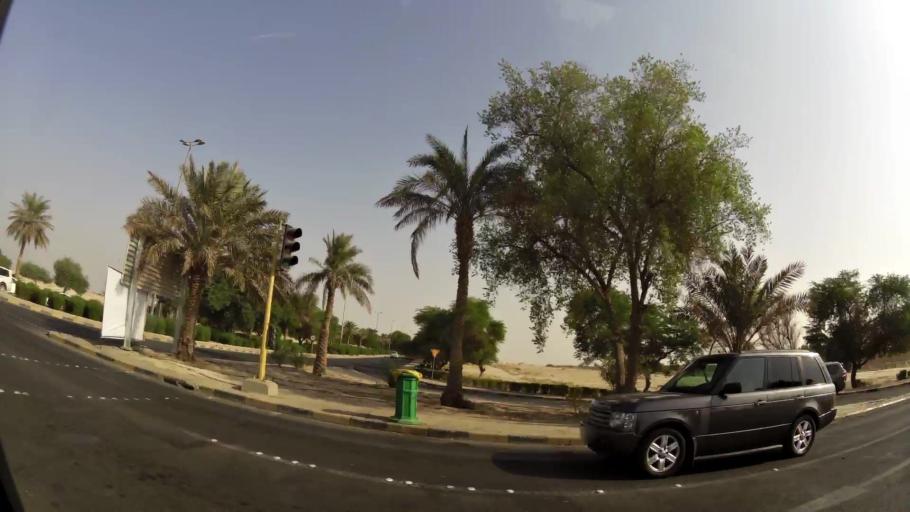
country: KW
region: Muhafazat al Jahra'
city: Al Jahra'
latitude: 29.3338
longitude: 47.7078
